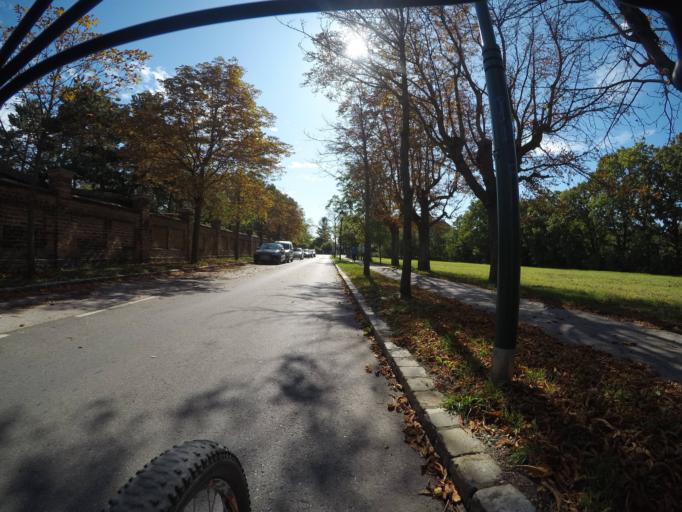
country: AT
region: Lower Austria
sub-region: Politischer Bezirk Modling
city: Modling
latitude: 48.0940
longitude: 16.2969
